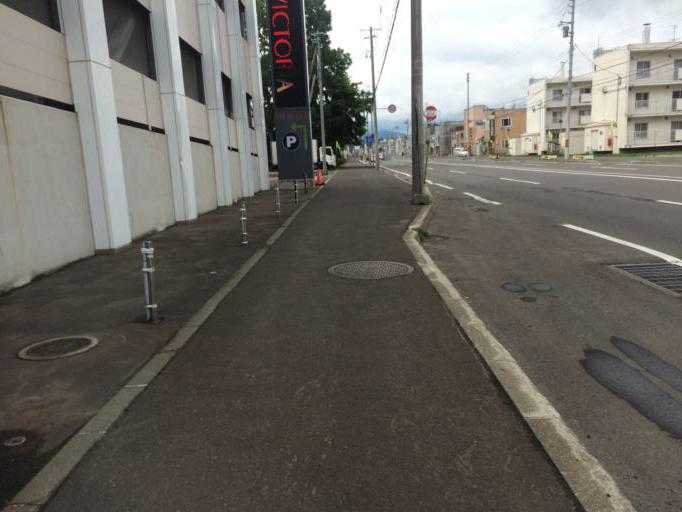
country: JP
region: Hokkaido
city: Niseko Town
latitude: 42.8967
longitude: 140.7520
